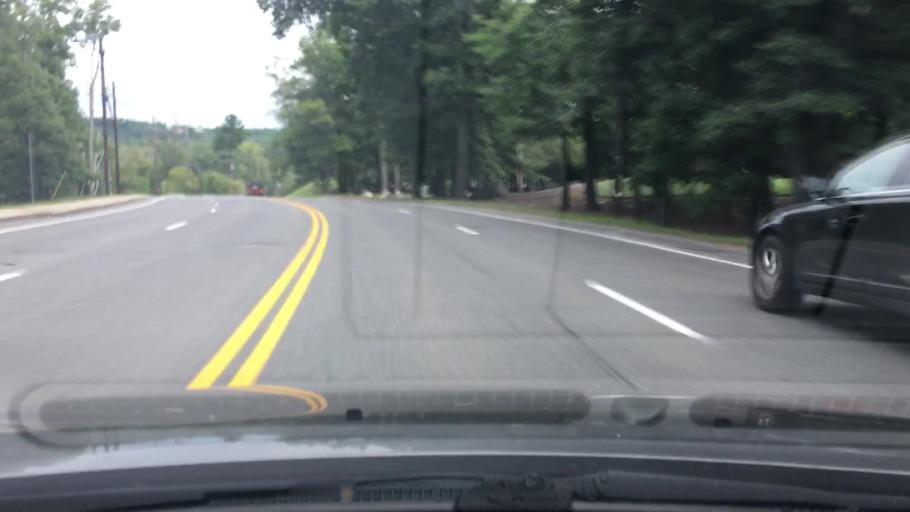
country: US
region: Massachusetts
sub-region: Middlesex County
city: Hopkinton
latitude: 42.2082
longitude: -71.5467
